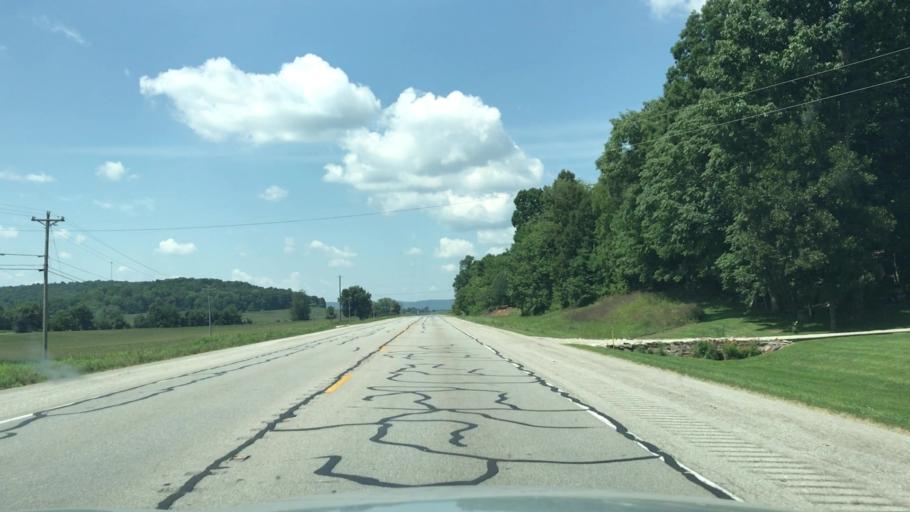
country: US
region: Kentucky
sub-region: Wayne County
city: Monticello
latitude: 36.7983
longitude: -84.9275
